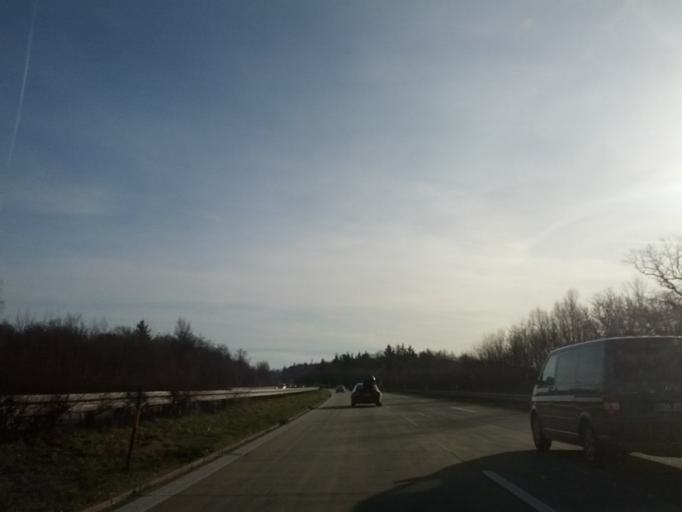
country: DE
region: Bavaria
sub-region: Regierungsbezirk Mittelfranken
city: Ohrenbach
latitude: 49.4924
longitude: 10.2018
